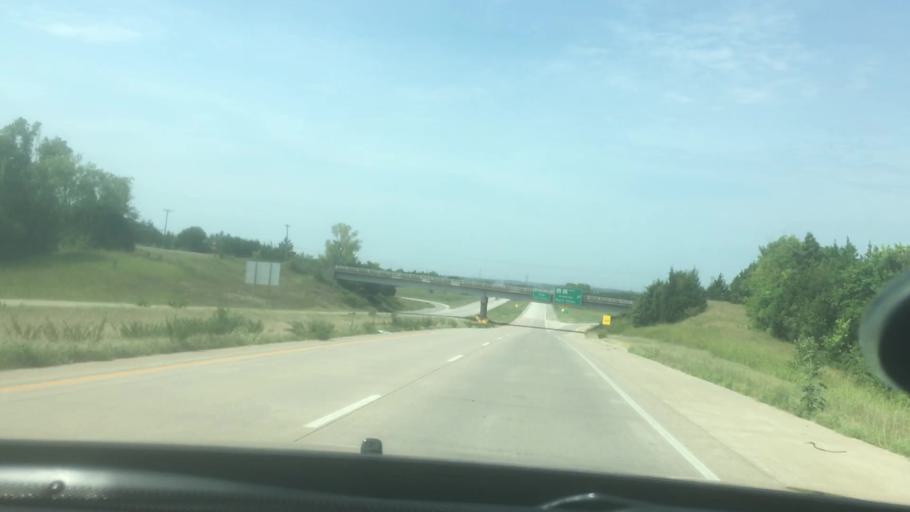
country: US
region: Oklahoma
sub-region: Pontotoc County
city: Ada
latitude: 34.7813
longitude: -96.6991
